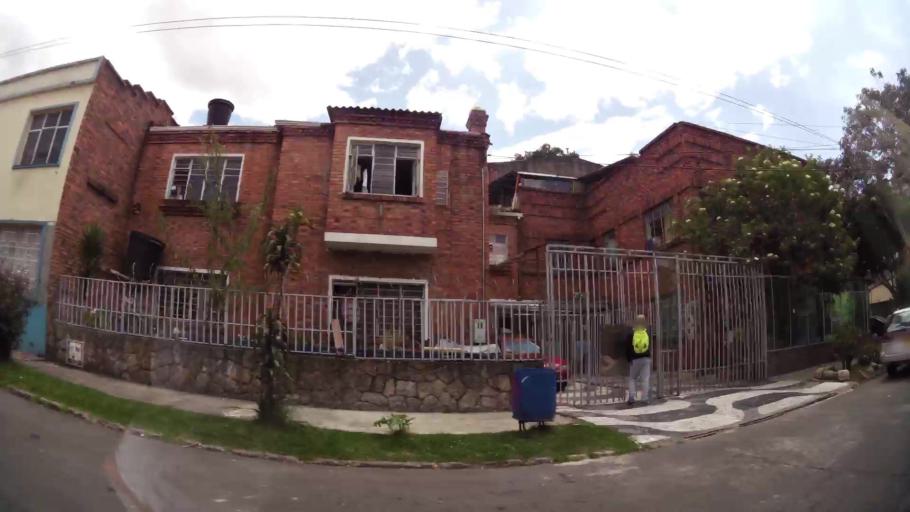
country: CO
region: Bogota D.C.
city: Bogota
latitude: 4.6327
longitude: -74.0733
